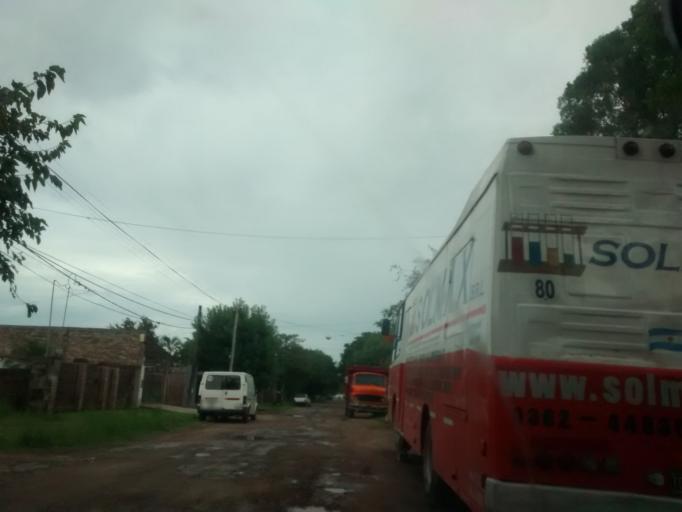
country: AR
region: Chaco
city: Resistencia
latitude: -27.4406
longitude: -58.9817
